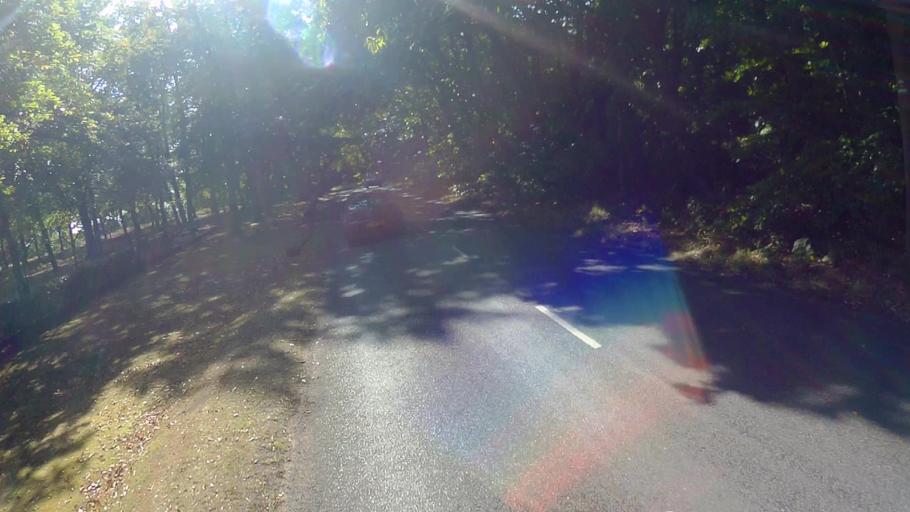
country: GB
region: England
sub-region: Surrey
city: Farnham
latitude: 51.1786
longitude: -0.7797
